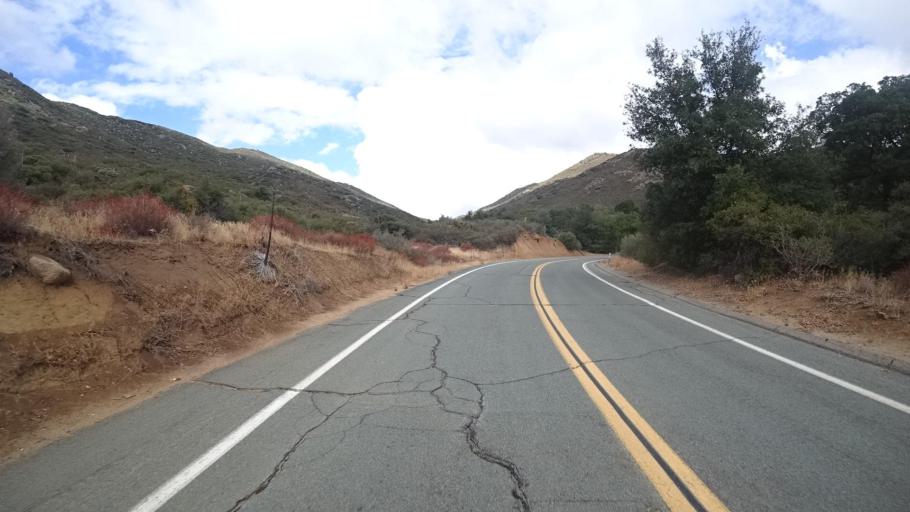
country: US
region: California
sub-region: San Diego County
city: Pine Valley
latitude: 32.7866
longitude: -116.4513
